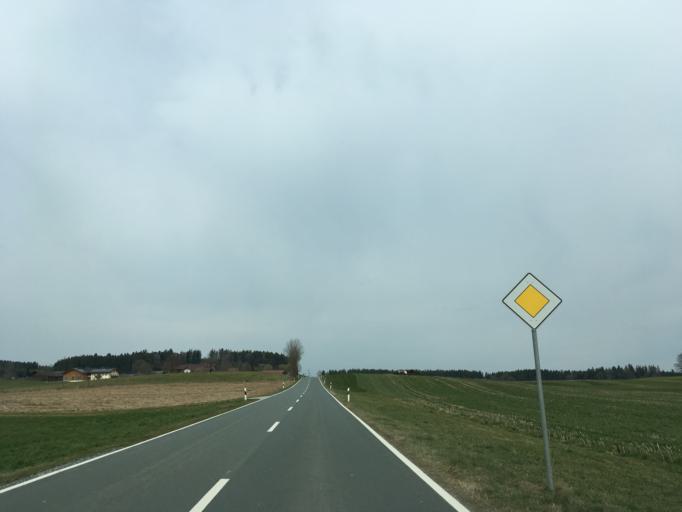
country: DE
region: Bavaria
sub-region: Upper Bavaria
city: Hoslwang
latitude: 47.9469
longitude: 12.3560
